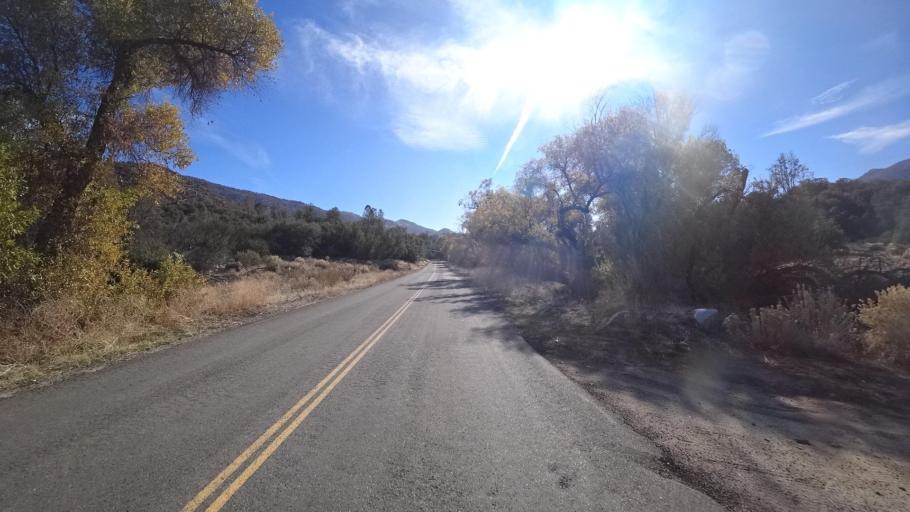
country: US
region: California
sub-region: Kern County
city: Bodfish
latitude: 35.4919
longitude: -118.5180
